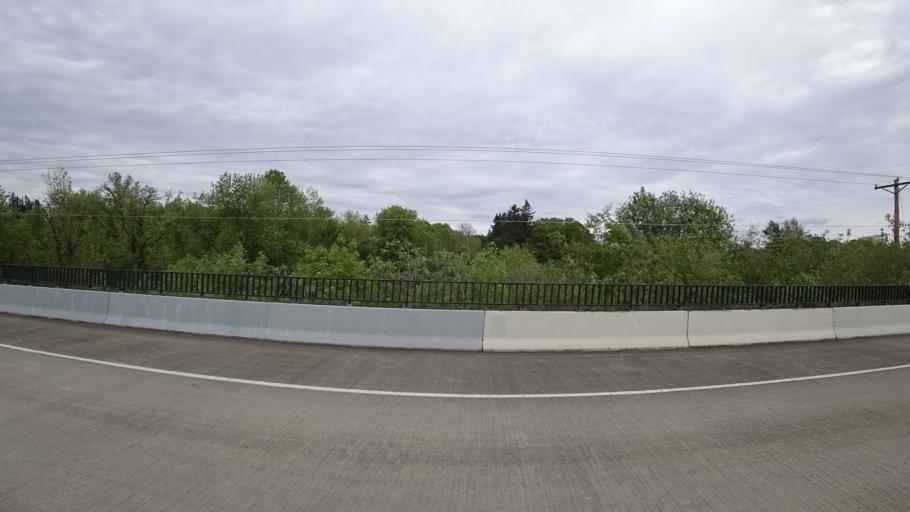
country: US
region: Oregon
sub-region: Washington County
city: Hillsboro
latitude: 45.4896
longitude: -122.9515
